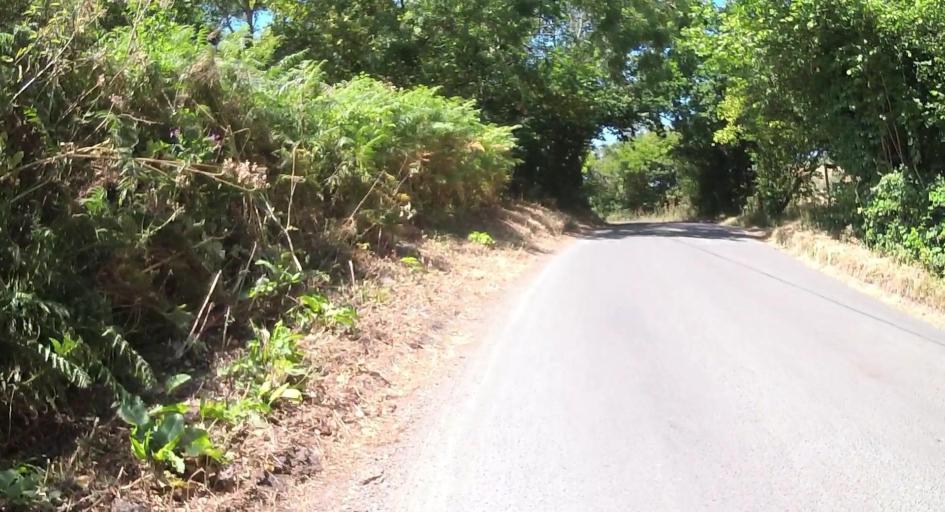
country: GB
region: England
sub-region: Dorset
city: Wareham
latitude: 50.6316
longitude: -2.1164
